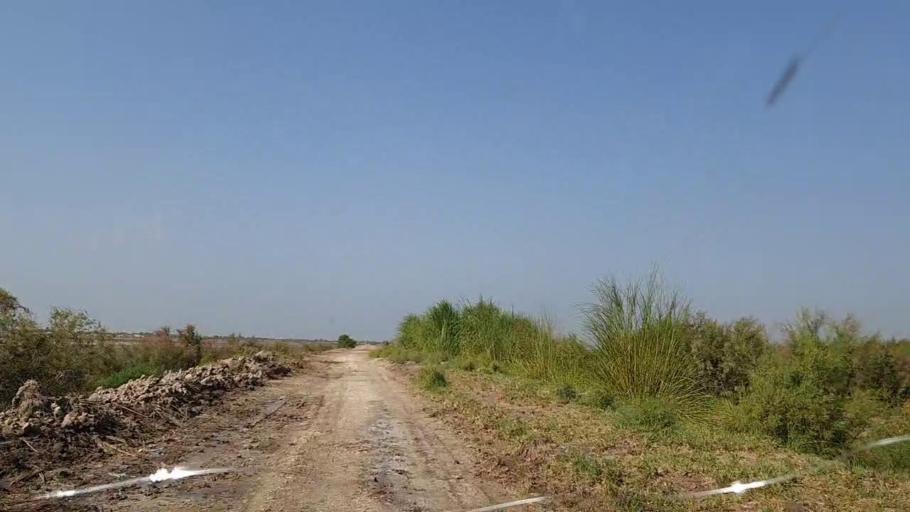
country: PK
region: Sindh
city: Khanpur
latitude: 27.6847
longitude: 69.3797
